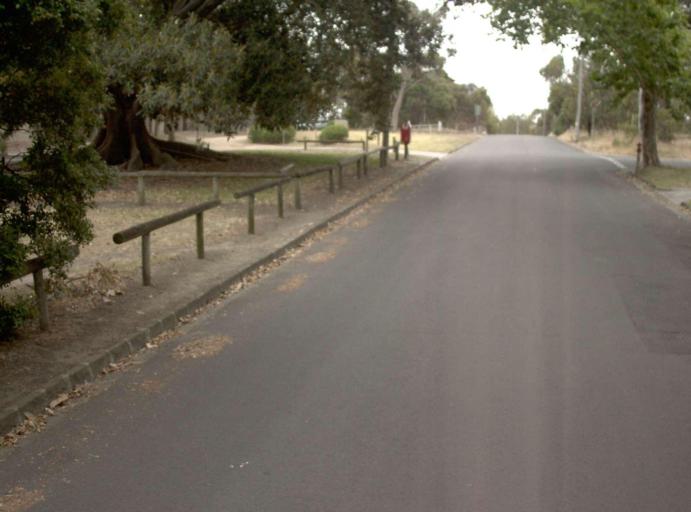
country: AU
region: Victoria
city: Abbotsford
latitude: -37.8051
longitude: 145.0110
